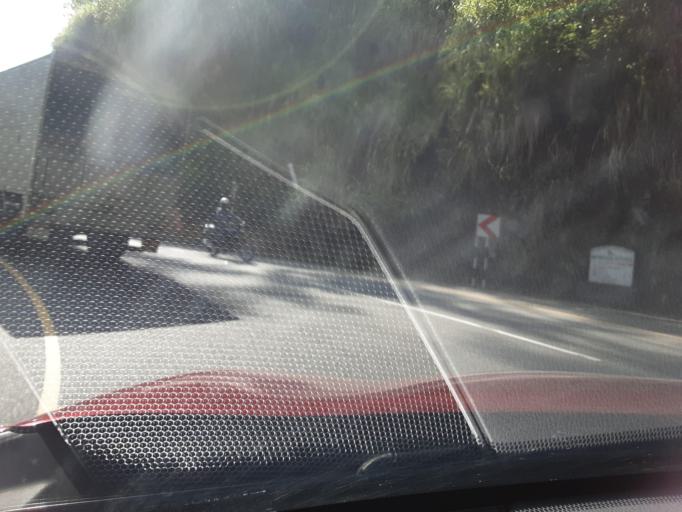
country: LK
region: Uva
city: Badulla
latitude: 6.9638
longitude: 81.0945
